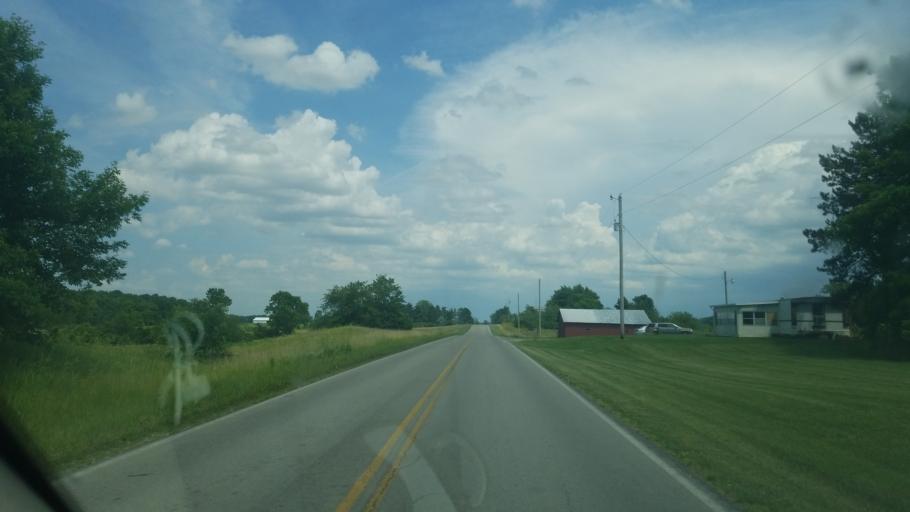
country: US
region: Ohio
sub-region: Logan County
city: Russells Point
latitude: 40.6159
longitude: -83.8403
